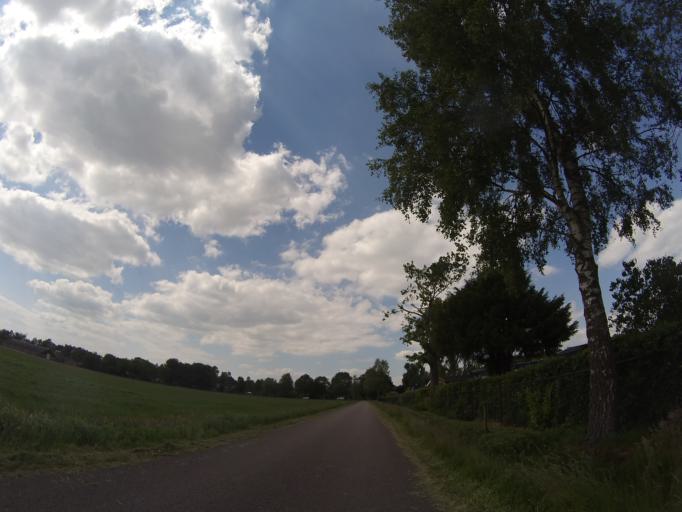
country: NL
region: Gelderland
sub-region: Gemeente Barneveld
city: Stroe
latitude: 52.1906
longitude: 5.6543
